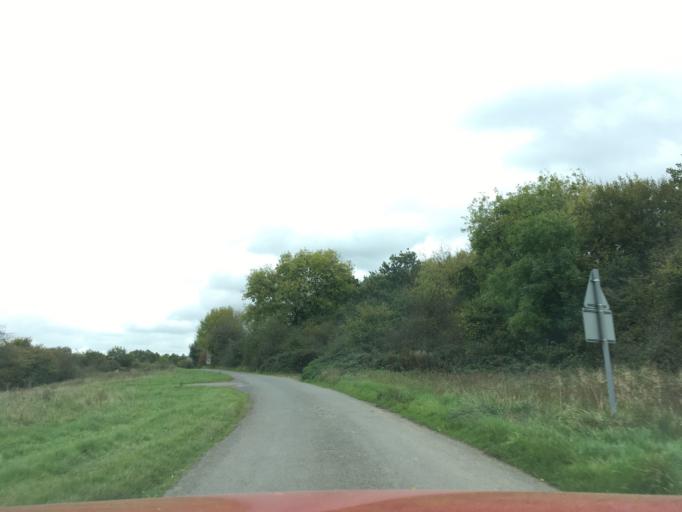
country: GB
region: England
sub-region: South Gloucestershire
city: Wickwar
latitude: 51.5971
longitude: -2.3740
